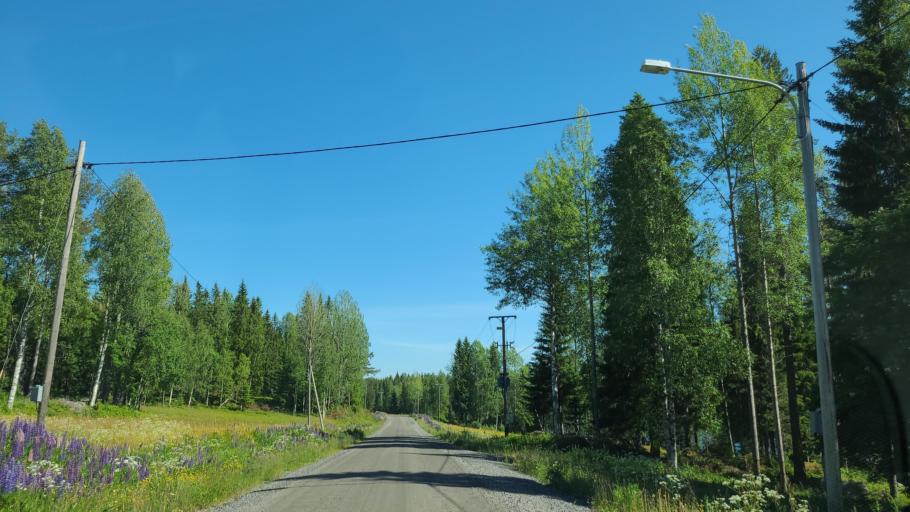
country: SE
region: Vaesterbotten
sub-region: Bjurholms Kommun
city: Bjurholm
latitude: 63.6402
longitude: 19.1419
